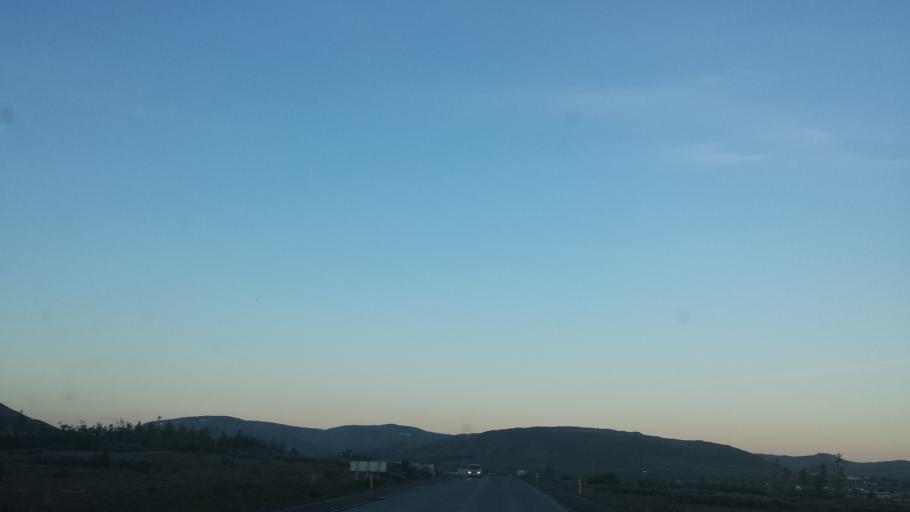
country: IS
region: Capital Region
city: Mosfellsbaer
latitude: 64.1957
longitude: -21.7015
